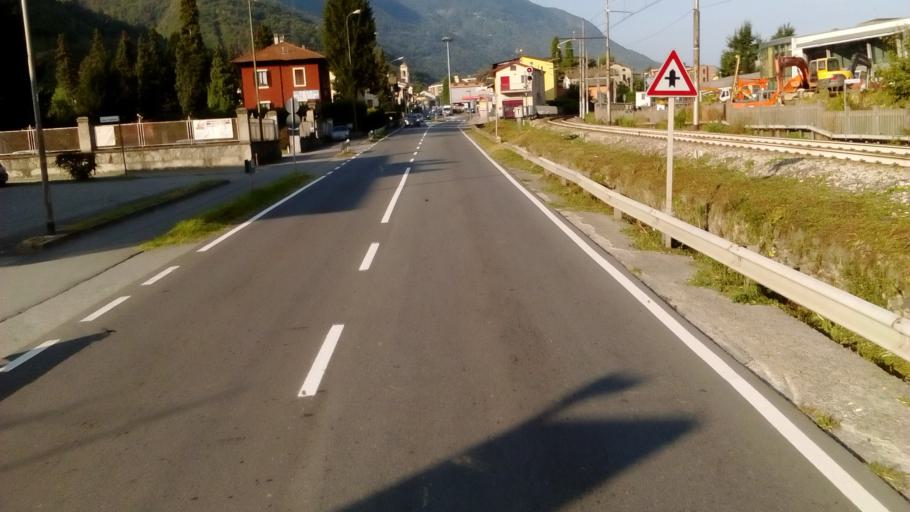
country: IT
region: Lombardy
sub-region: Provincia di Sondrio
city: Morbegno
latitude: 46.1353
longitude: 9.5833
